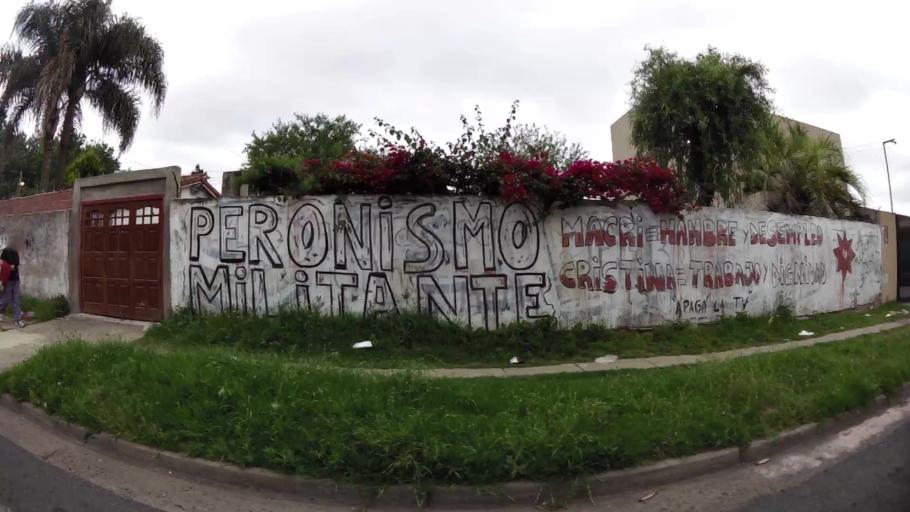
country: AR
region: Buenos Aires
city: San Justo
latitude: -34.7183
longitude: -58.5306
